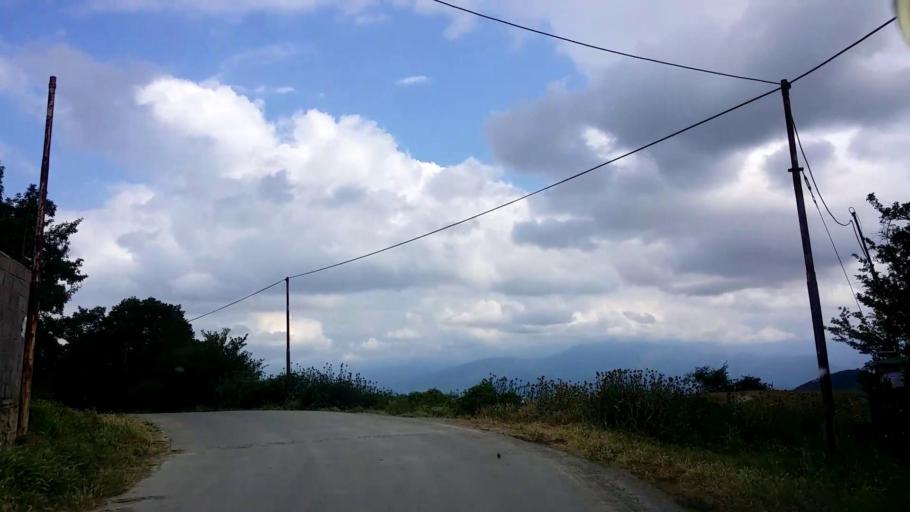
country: IR
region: Mazandaran
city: Chalus
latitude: 36.5543
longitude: 51.2770
